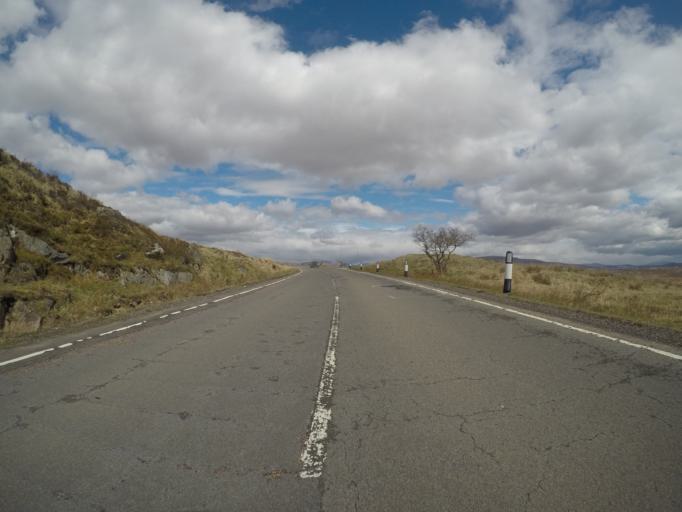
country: GB
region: Scotland
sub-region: Highland
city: Spean Bridge
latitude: 56.6216
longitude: -4.7656
